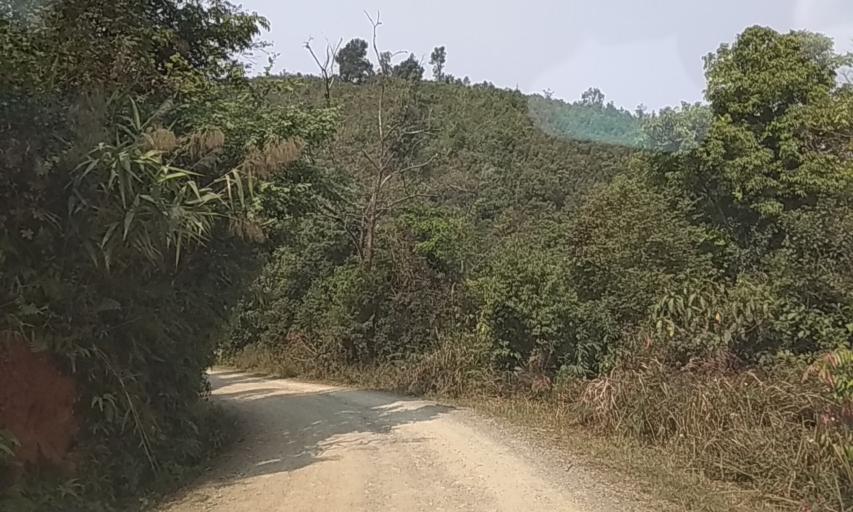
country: TH
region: Nan
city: Chaloem Phra Kiat
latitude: 20.0523
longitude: 101.0808
